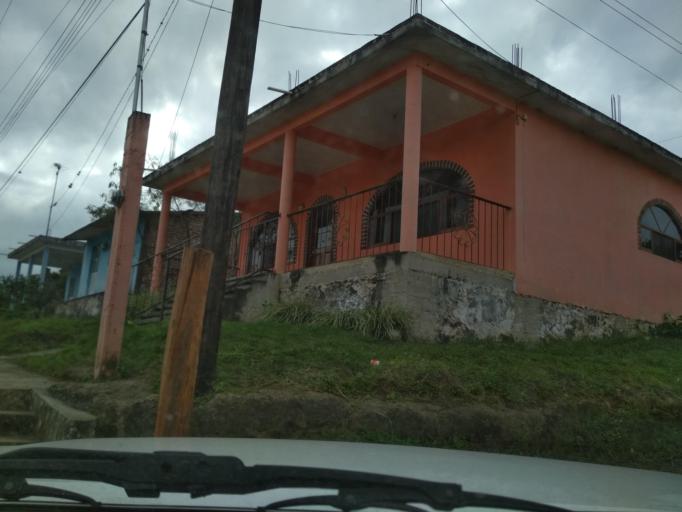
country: MX
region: Veracruz
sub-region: Coatepec
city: Tuzamapan
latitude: 19.3693
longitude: -96.8826
